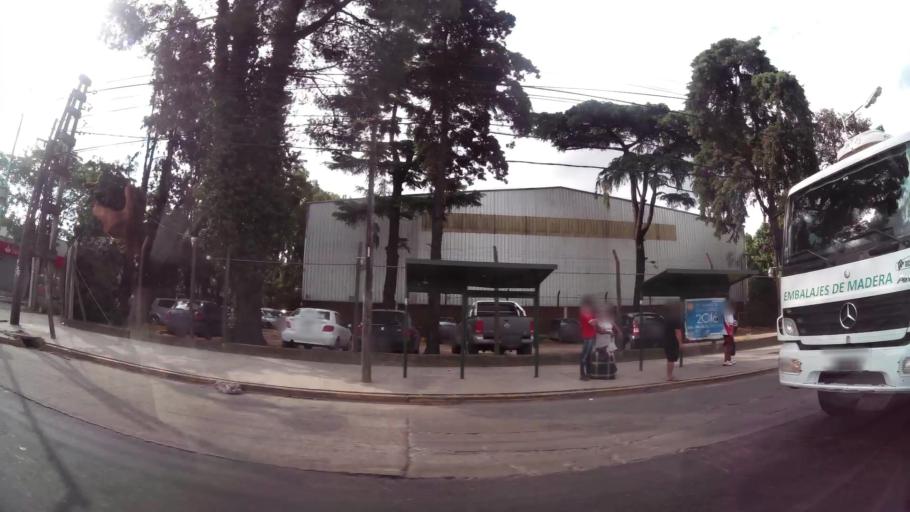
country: AR
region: Buenos Aires
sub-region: Partido de Tigre
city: Tigre
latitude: -34.4727
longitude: -58.6576
